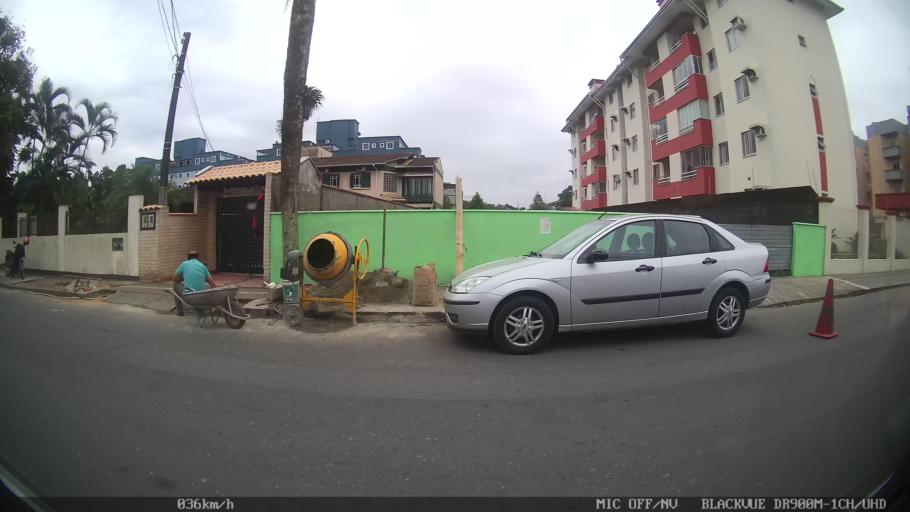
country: BR
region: Santa Catarina
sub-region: Joinville
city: Joinville
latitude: -26.2660
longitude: -48.8585
